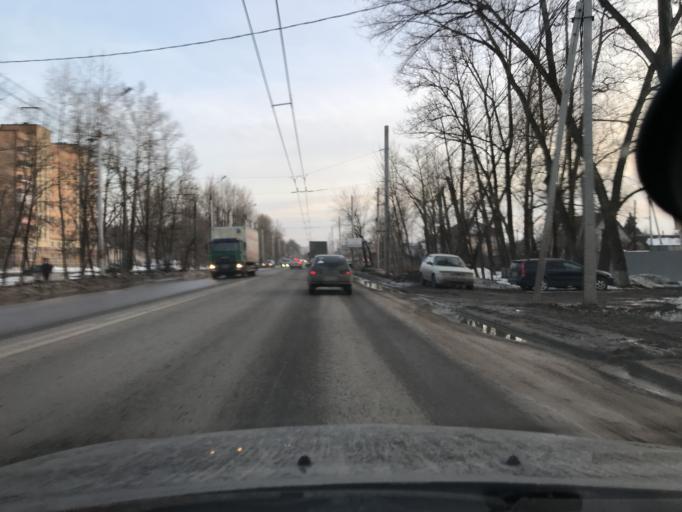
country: RU
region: Kaluga
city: Kaluga
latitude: 54.6007
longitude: 36.2626
